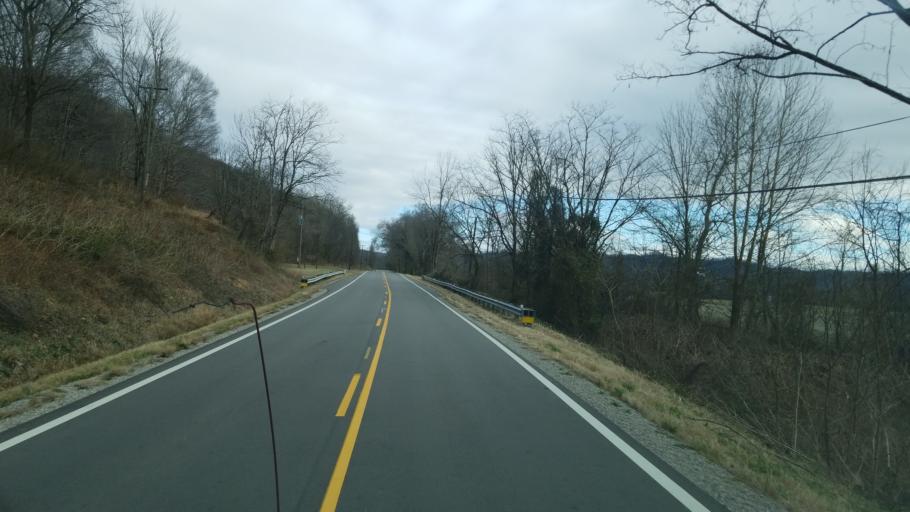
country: US
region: Kentucky
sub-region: Lewis County
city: Vanceburg
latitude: 38.6263
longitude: -83.1998
